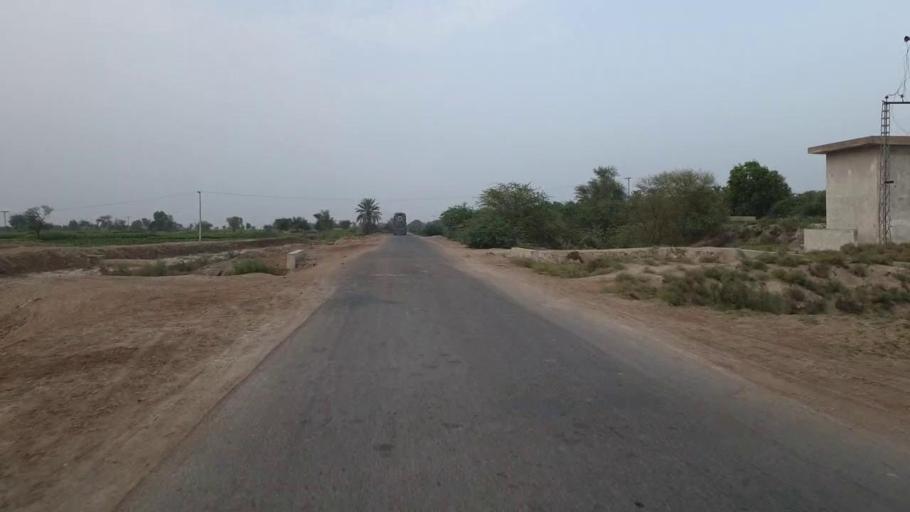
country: PK
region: Sindh
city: Daur
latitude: 26.4338
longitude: 68.2691
